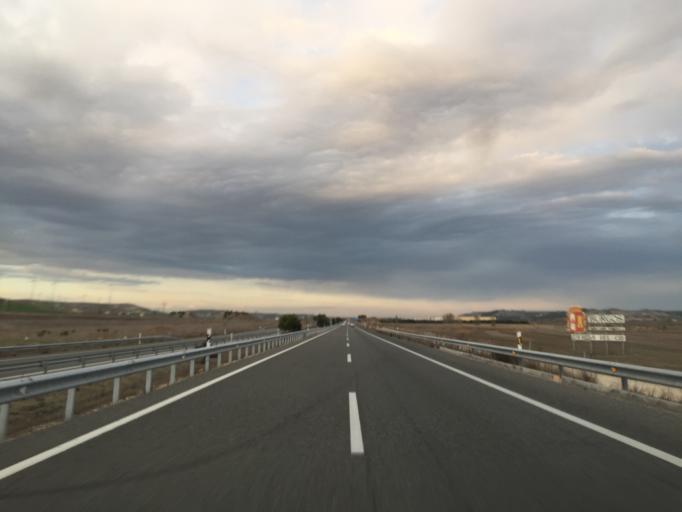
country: ES
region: Castille and Leon
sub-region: Provincia de Burgos
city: Villazopeque
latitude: 42.1902
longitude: -4.0337
